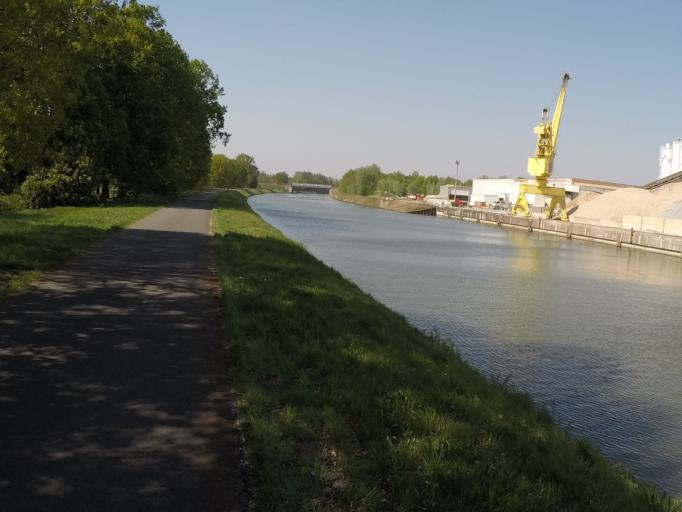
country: BE
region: Flanders
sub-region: Provincie Antwerpen
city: Lier
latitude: 51.1380
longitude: 4.5869
